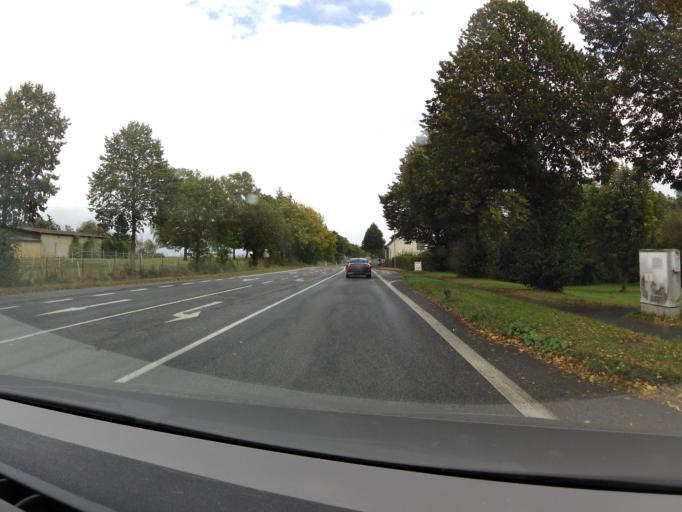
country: DE
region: Lower Saxony
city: Hardegsen
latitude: 51.6420
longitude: 9.8710
